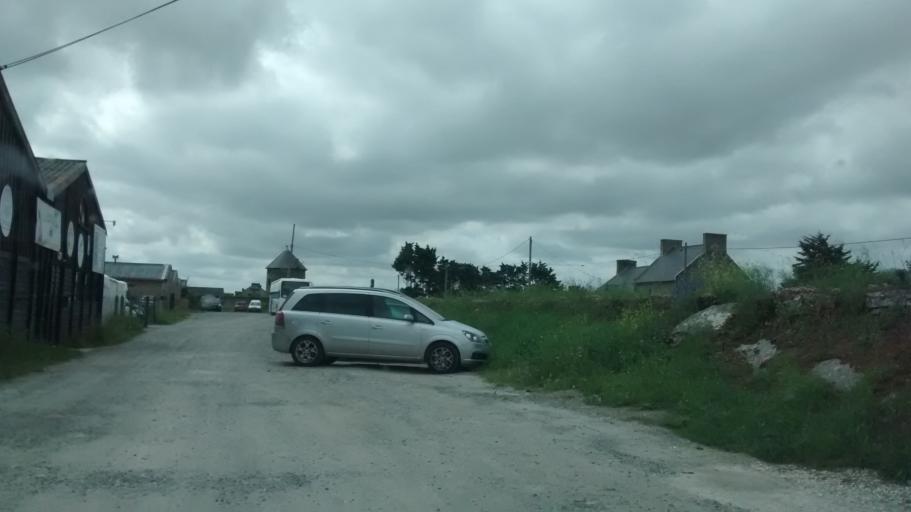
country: FR
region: Brittany
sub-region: Departement d'Ille-et-Vilaine
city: Saint-Meloir-des-Ondes
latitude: 48.6354
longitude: -1.8665
